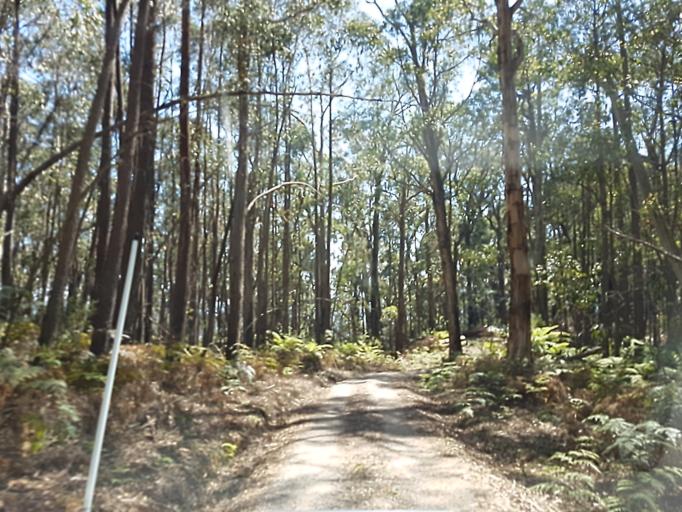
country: AU
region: Victoria
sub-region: East Gippsland
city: Lakes Entrance
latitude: -37.2910
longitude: 148.3206
